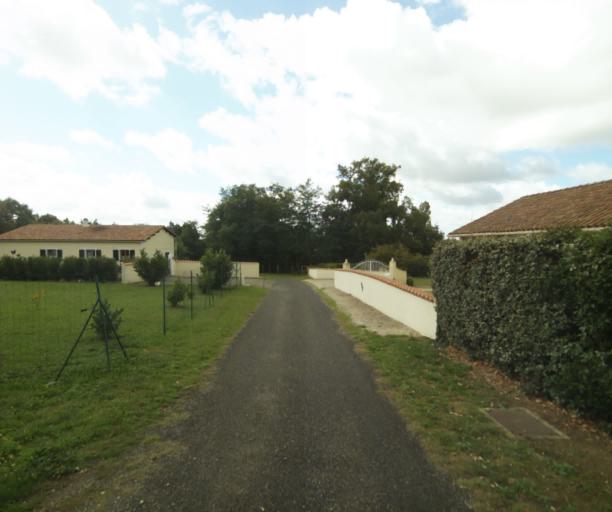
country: FR
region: Midi-Pyrenees
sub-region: Departement du Gers
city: Nogaro
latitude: 43.8189
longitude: -0.0862
